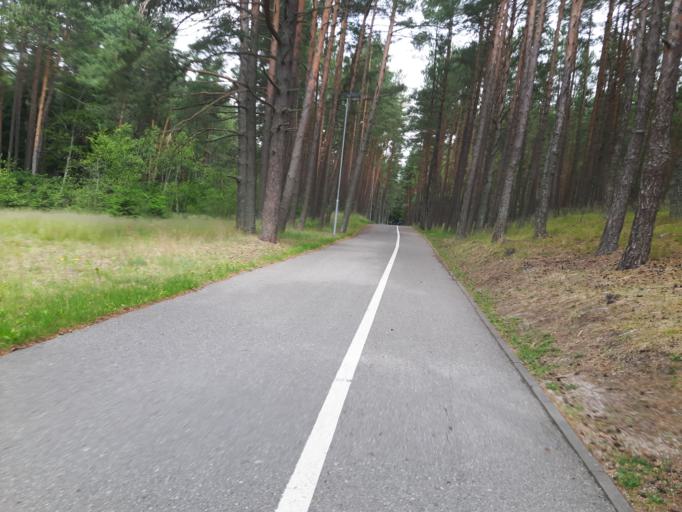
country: LT
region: Klaipedos apskritis
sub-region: Klaipeda
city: Klaipeda
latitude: 55.7462
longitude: 21.1204
